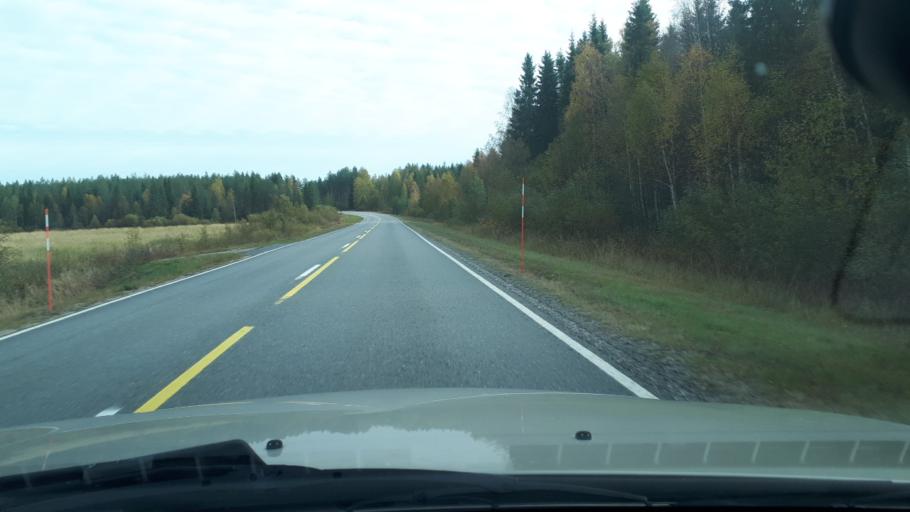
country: FI
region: Lapland
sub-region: Rovaniemi
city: Ranua
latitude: 65.9655
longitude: 25.9929
